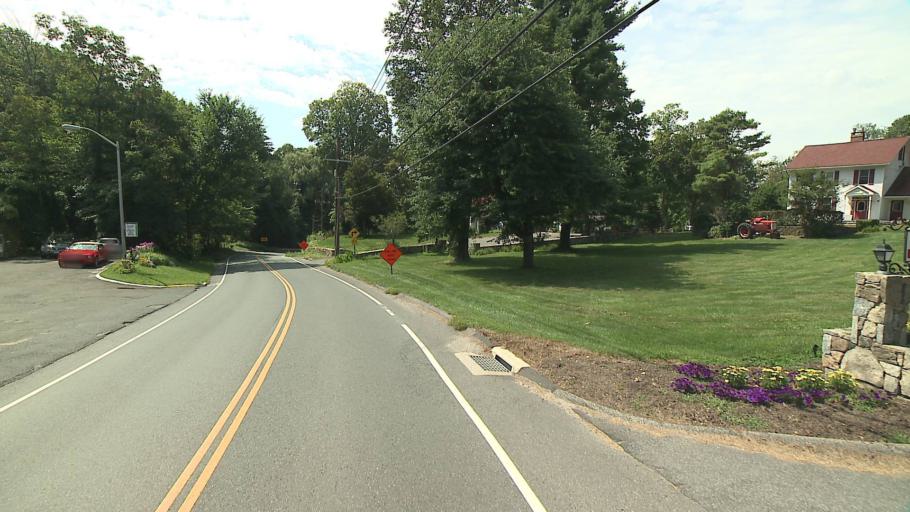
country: US
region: New York
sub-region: Putnam County
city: Putnam Lake
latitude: 41.4701
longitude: -73.4715
